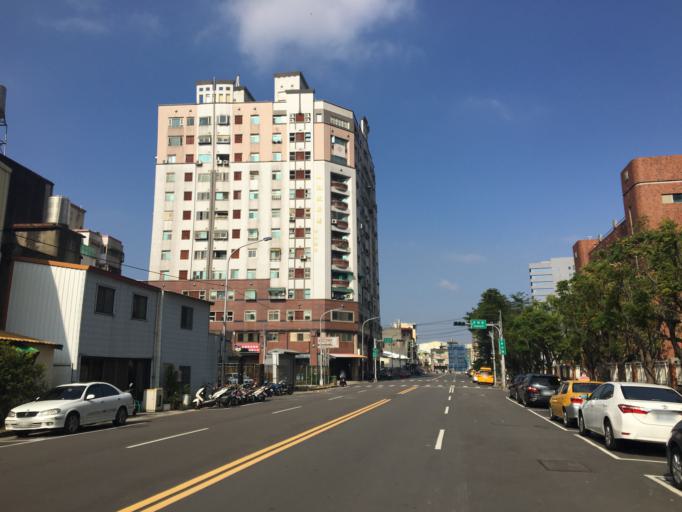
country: TW
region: Taiwan
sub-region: Hsinchu
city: Hsinchu
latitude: 24.8027
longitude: 120.9890
